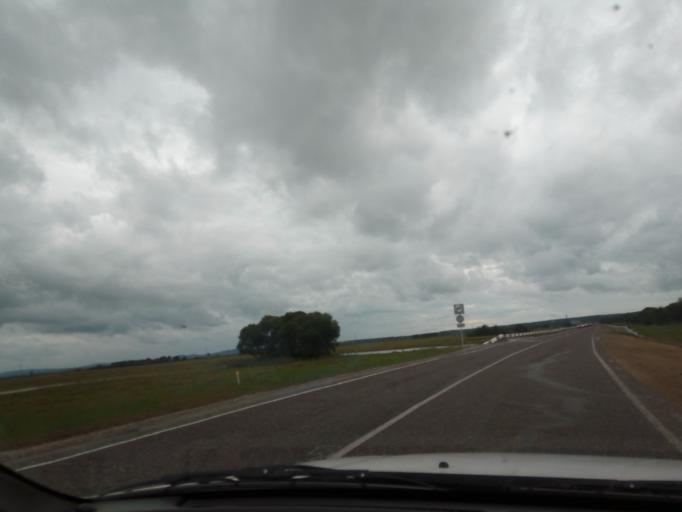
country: RU
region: Primorskiy
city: Dal'nerechensk
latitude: 45.9155
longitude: 133.7711
